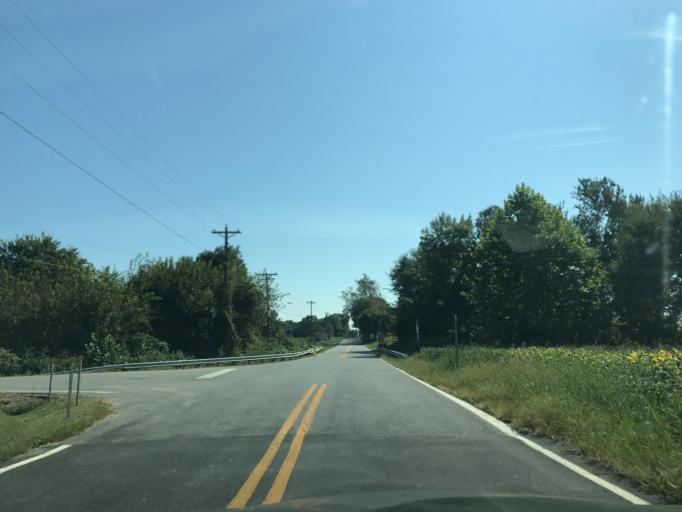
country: US
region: Maryland
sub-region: Queen Anne's County
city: Kingstown
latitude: 39.2774
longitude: -75.9210
